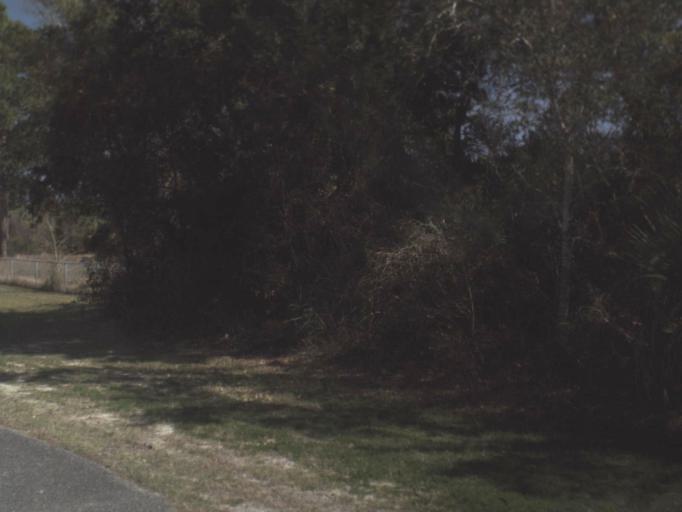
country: US
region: Florida
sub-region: Franklin County
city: Eastpoint
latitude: 29.7360
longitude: -84.8924
